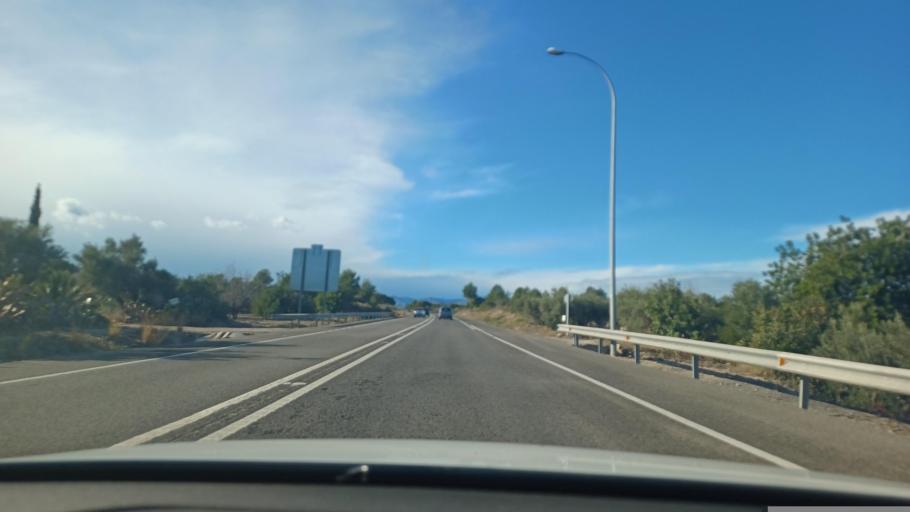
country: ES
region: Catalonia
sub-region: Provincia de Tarragona
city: l'Ametlla de Mar
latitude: 40.8937
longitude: 0.7773
